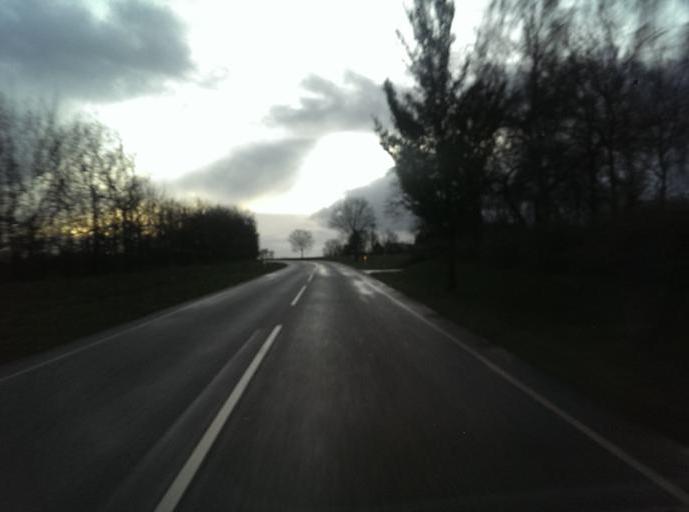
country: DK
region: South Denmark
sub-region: Esbjerg Kommune
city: Bramming
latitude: 55.4591
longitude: 8.6896
